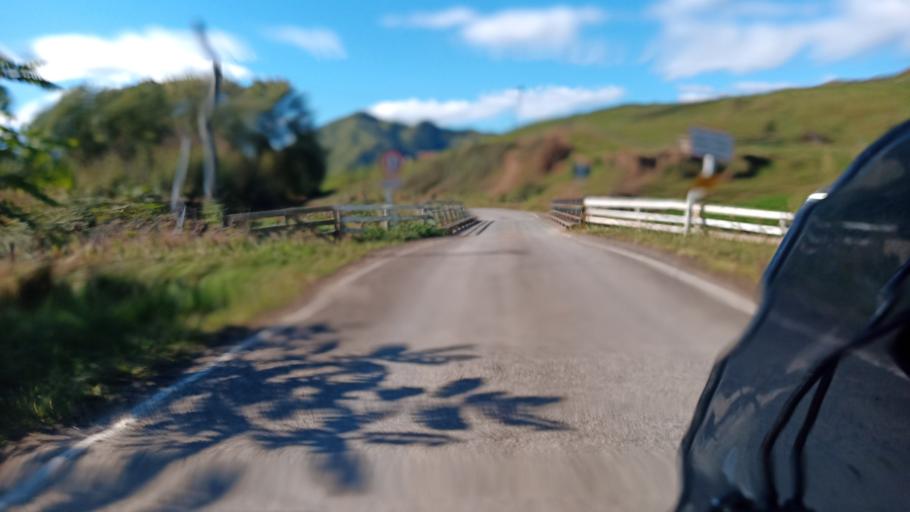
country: NZ
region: Bay of Plenty
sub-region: Opotiki District
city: Opotiki
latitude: -38.2586
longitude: 177.5686
